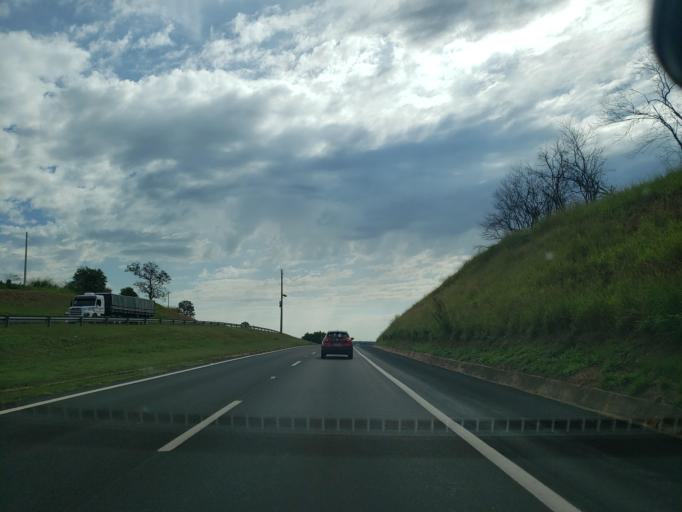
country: BR
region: Sao Paulo
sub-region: Cafelandia
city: Cafelandia
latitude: -21.7980
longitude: -49.6440
